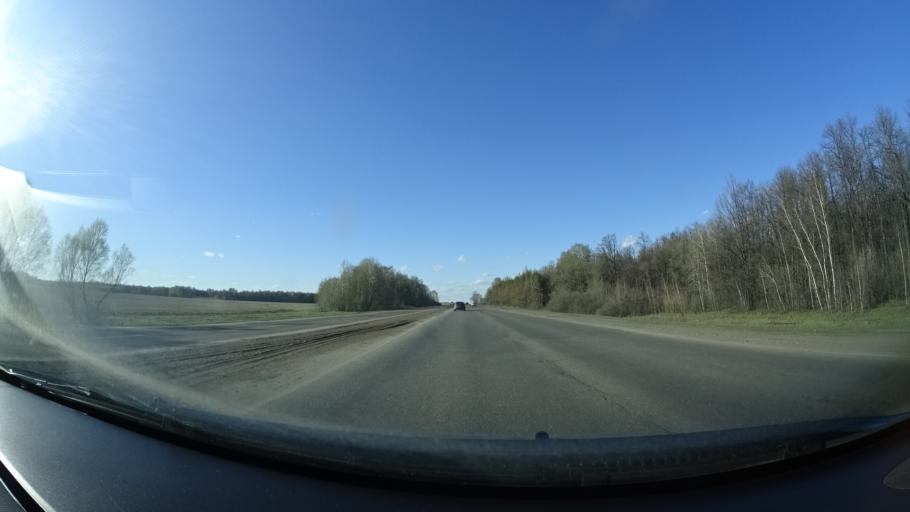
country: RU
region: Bashkortostan
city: Kabakovo
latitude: 54.4537
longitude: 55.9177
